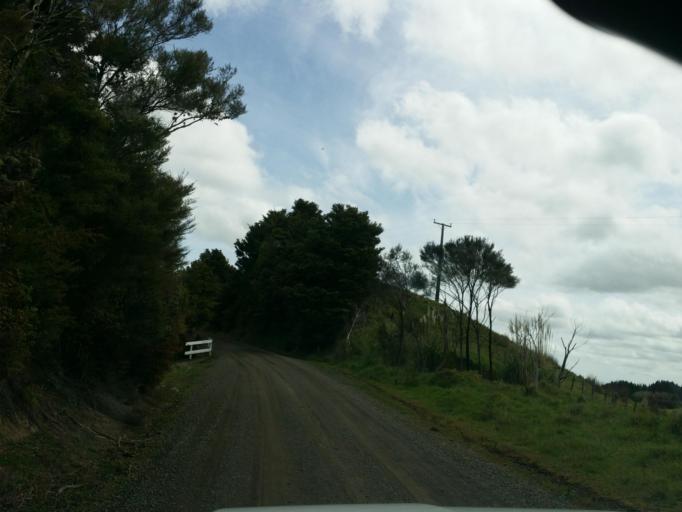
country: NZ
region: Northland
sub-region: Kaipara District
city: Dargaville
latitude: -35.9165
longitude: 174.0247
